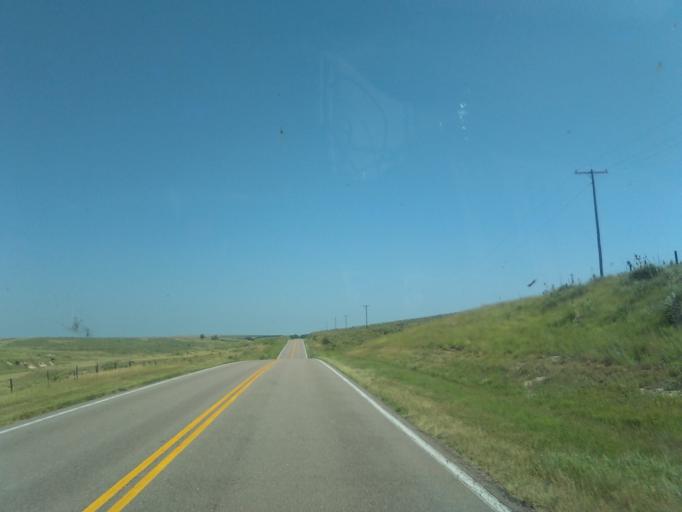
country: US
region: Nebraska
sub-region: Dundy County
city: Benkelman
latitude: 39.8755
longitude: -101.5411
